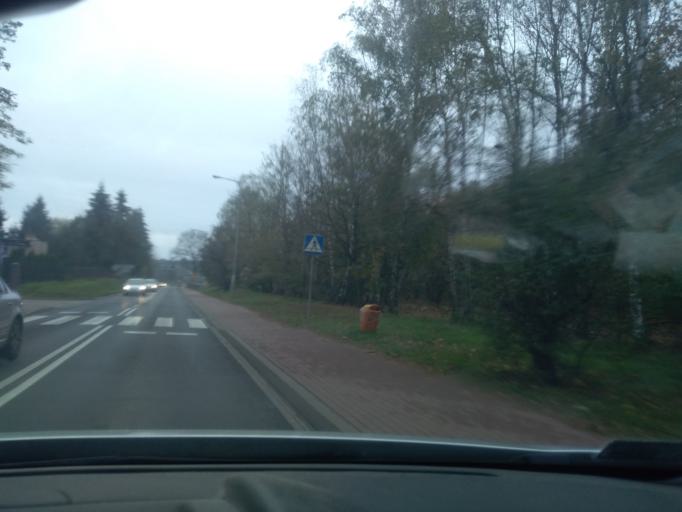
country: PL
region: Greater Poland Voivodeship
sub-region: Powiat poznanski
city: Murowana Goslina
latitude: 52.5411
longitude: 16.9689
